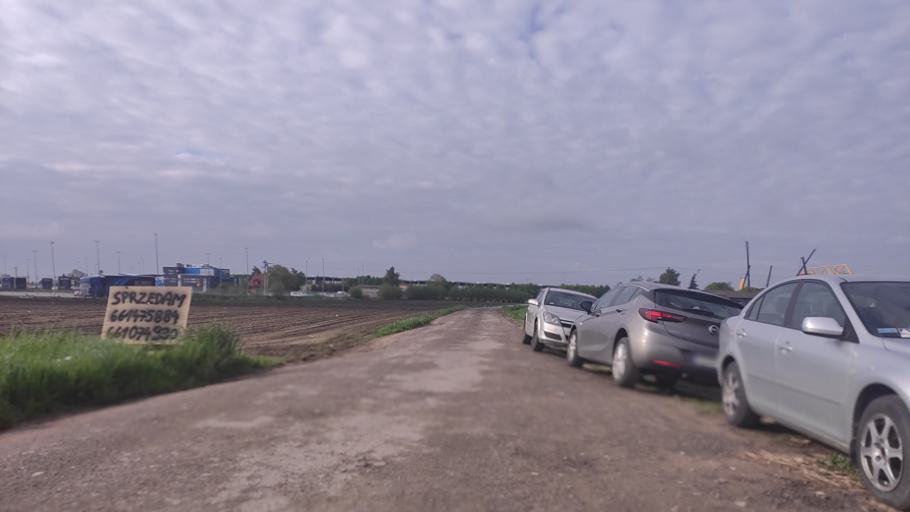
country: PL
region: Greater Poland Voivodeship
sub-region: Powiat poznanski
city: Swarzedz
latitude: 52.4028
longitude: 17.1393
